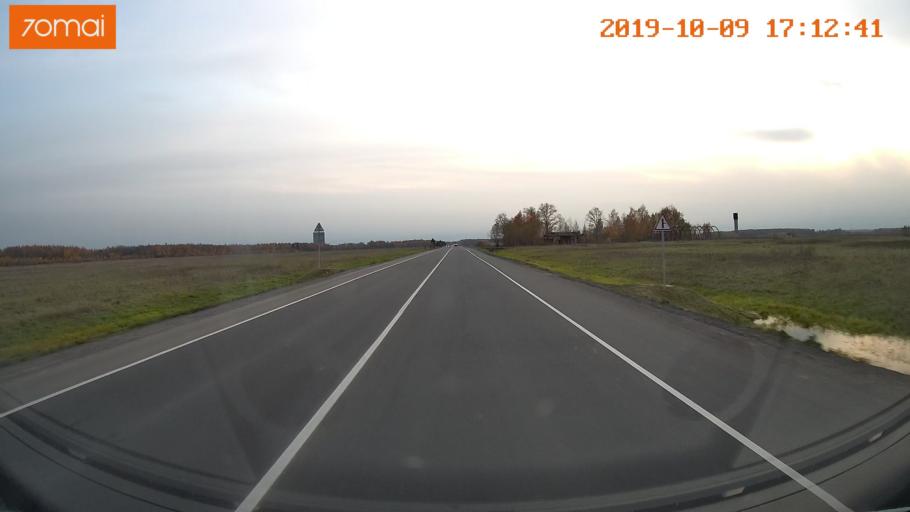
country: RU
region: Ivanovo
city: Privolzhsk
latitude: 57.3254
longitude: 41.2378
